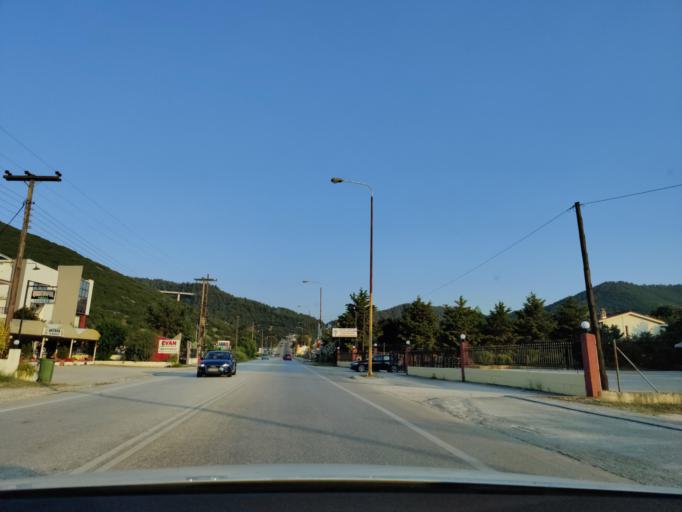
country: GR
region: East Macedonia and Thrace
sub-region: Nomos Kavalas
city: Amygdaleonas
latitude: 40.9571
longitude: 24.3641
